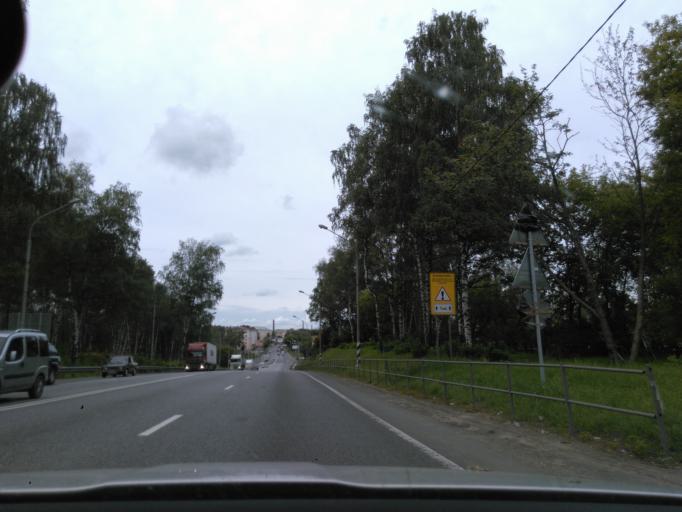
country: RU
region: Moskovskaya
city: Klin
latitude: 56.3285
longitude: 36.7423
